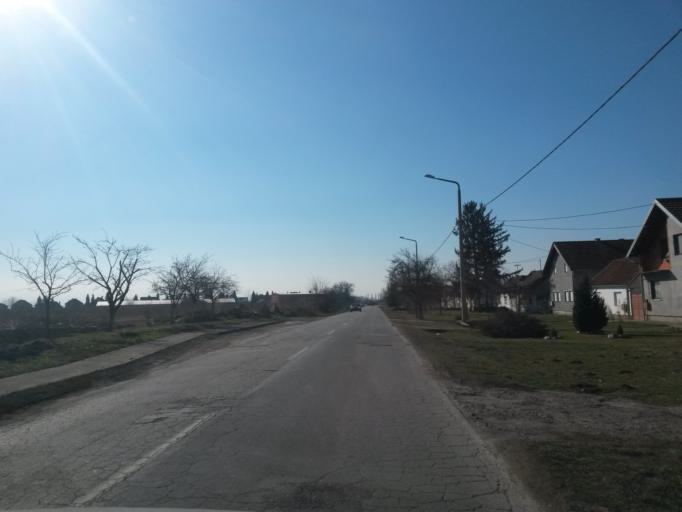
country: HR
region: Vukovarsko-Srijemska
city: Vukovar
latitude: 45.3301
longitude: 18.9952
